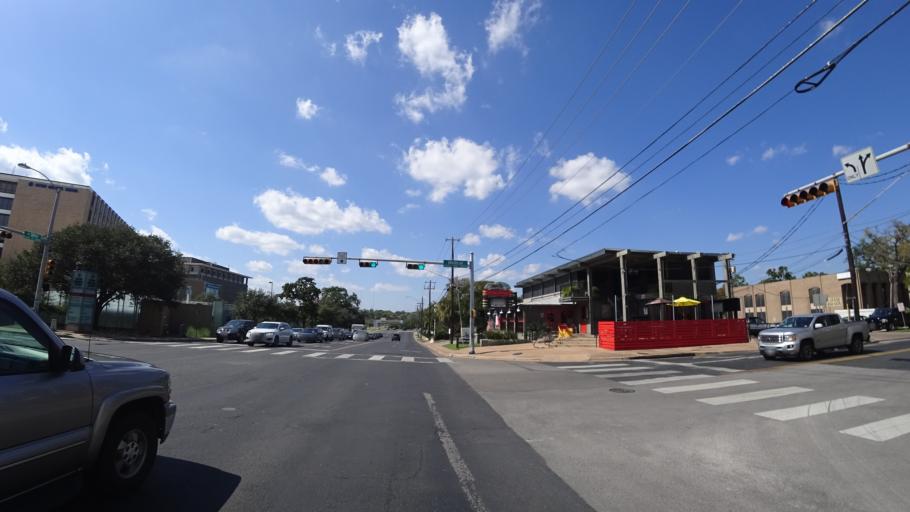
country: US
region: Texas
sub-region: Travis County
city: Austin
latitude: 30.3057
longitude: -97.7440
